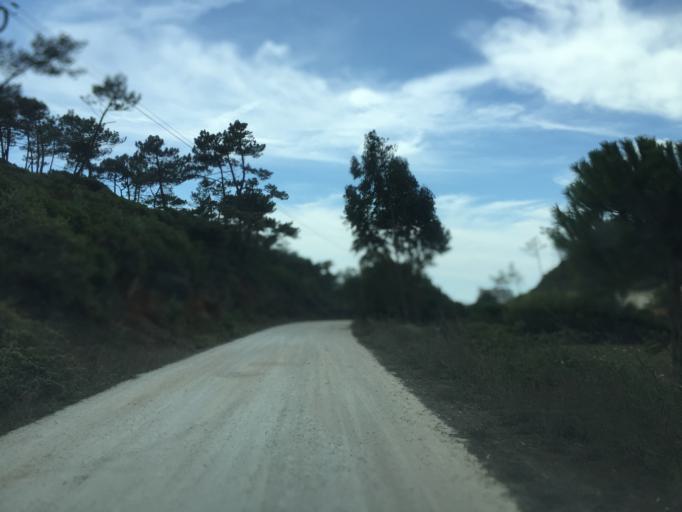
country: PT
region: Lisbon
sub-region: Torres Vedras
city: A dos Cunhados
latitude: 39.1834
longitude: -9.3411
